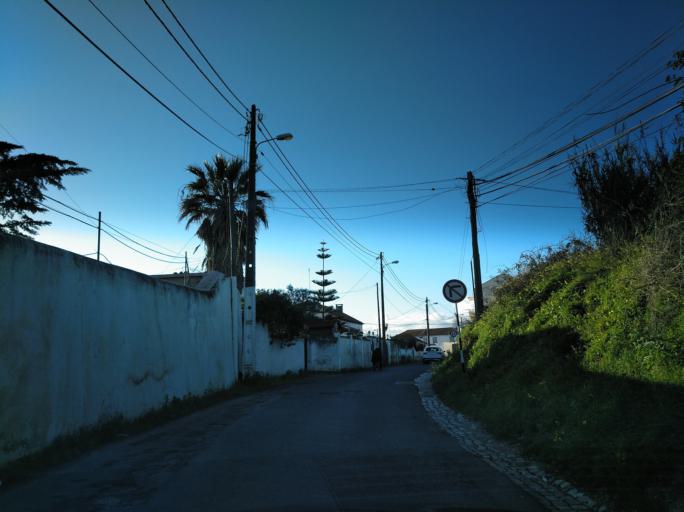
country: PT
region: Setubal
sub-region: Almada
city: Sobreda
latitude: 38.6464
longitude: -9.1908
